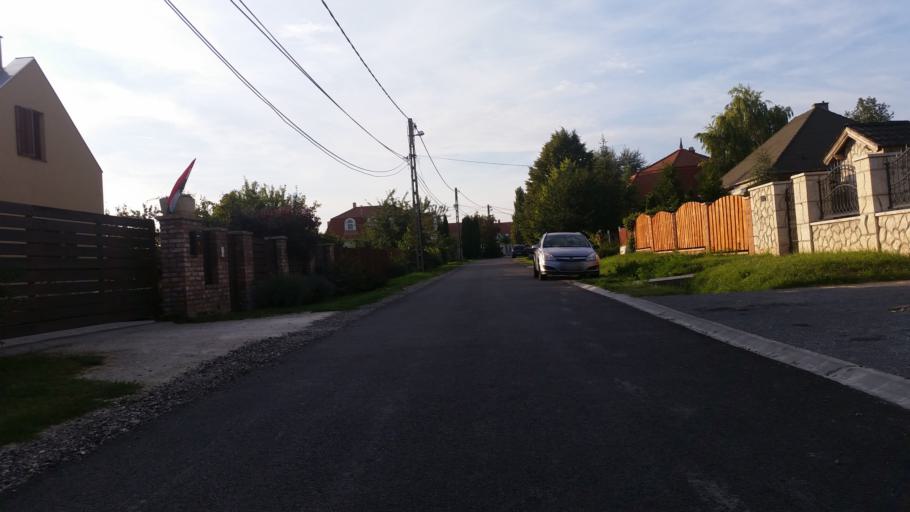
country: HU
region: Pest
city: Telki
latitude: 47.5576
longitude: 18.8064
